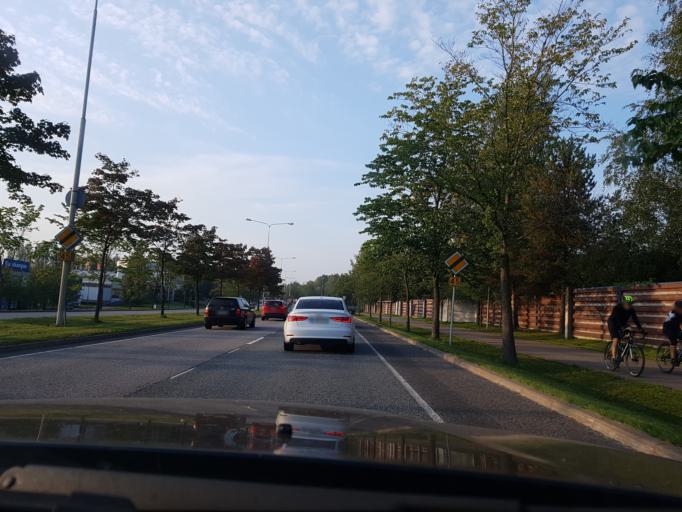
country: FI
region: Uusimaa
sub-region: Helsinki
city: Tuusula
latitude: 60.3869
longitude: 25.0253
